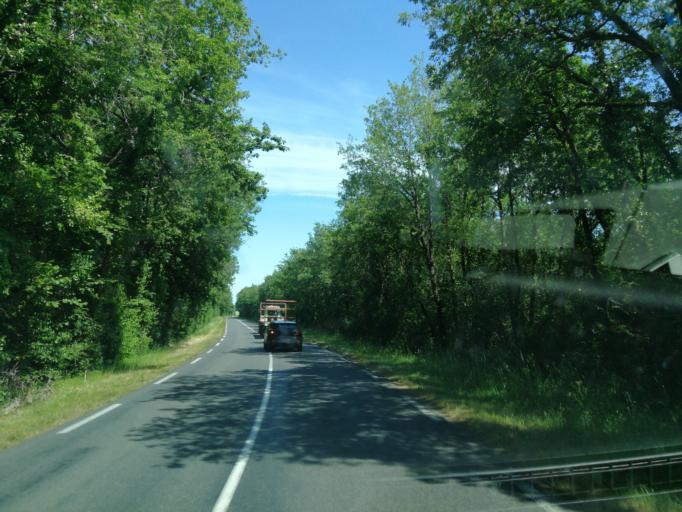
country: FR
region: Poitou-Charentes
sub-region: Departement des Deux-Sevres
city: Louzy
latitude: 46.9720
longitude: -0.1679
